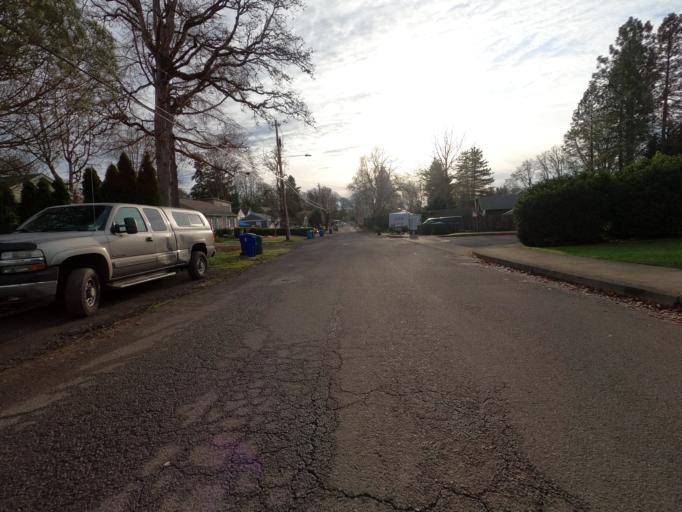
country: US
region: Oregon
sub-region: Clackamas County
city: Jennings Lodge
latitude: 45.3958
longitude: -122.6118
